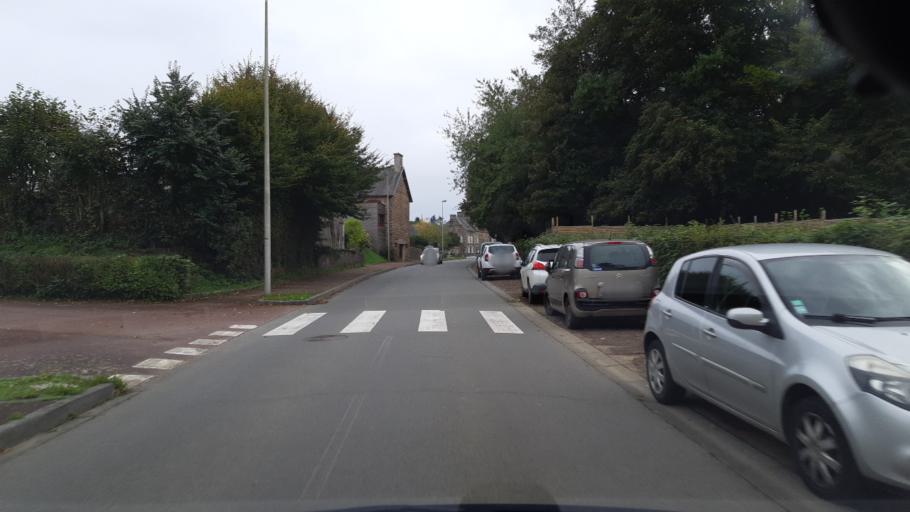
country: FR
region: Lower Normandy
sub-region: Departement de la Manche
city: Hambye
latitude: 48.9498
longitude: -1.2646
